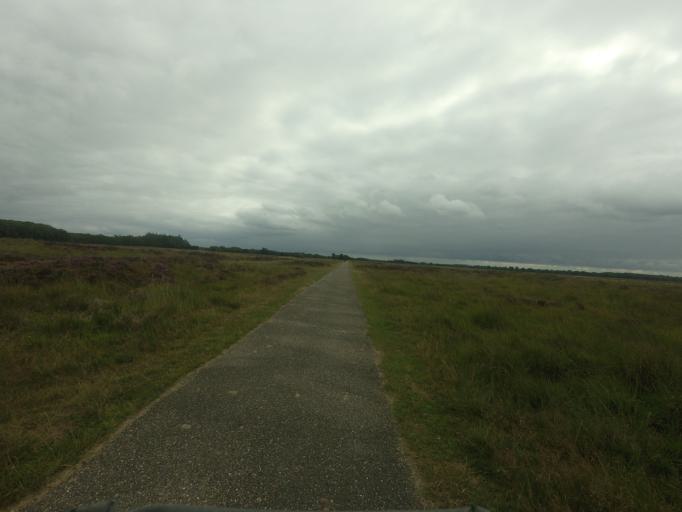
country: NL
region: Friesland
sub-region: Gemeente Weststellingwerf
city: Noordwolde
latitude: 52.9064
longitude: 6.2571
